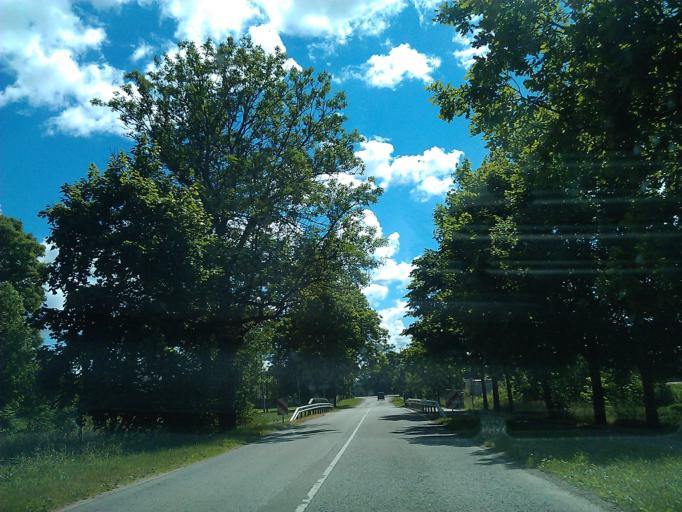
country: LV
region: Varaklani
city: Varaklani
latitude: 56.6055
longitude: 26.7712
